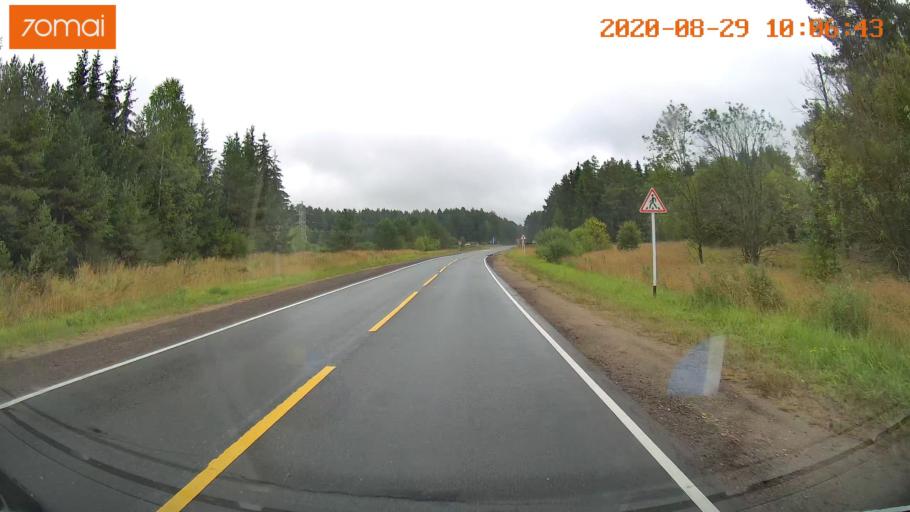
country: RU
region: Ivanovo
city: Kuznechikha
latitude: 57.3869
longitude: 42.5520
